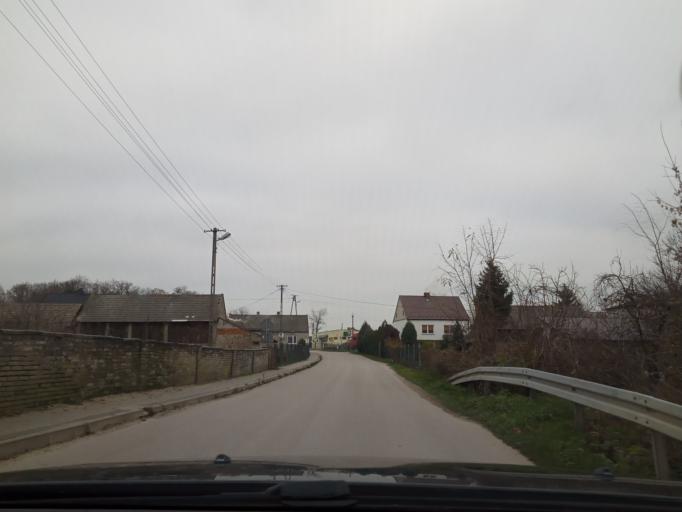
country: PL
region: Swietokrzyskie
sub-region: Powiat jedrzejowski
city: Imielno
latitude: 50.6021
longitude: 20.4905
